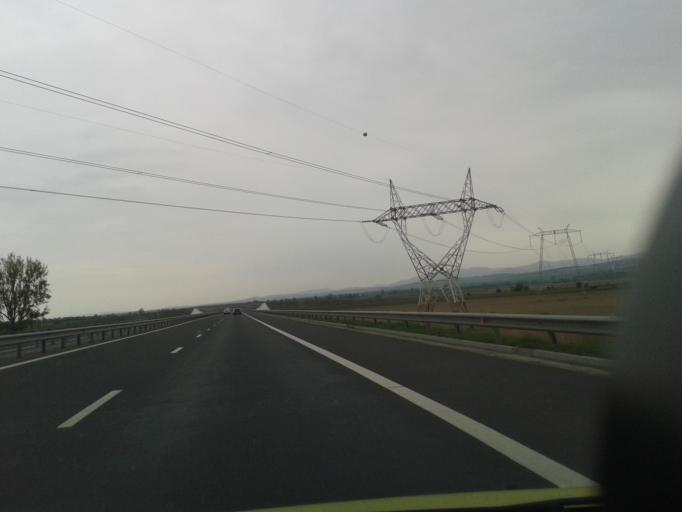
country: RO
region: Hunedoara
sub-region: Comuna Geoagiu
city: Geoagiu
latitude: 45.8804
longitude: 23.2086
